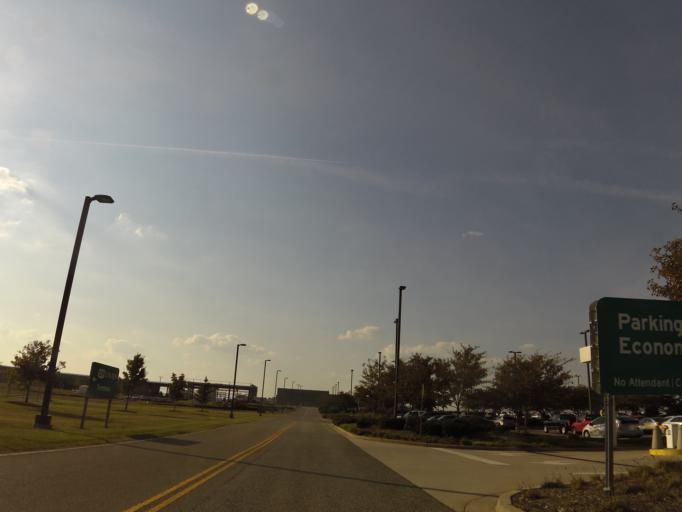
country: US
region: Tennessee
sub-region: Blount County
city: Alcoa
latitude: 35.8027
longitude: -83.9925
